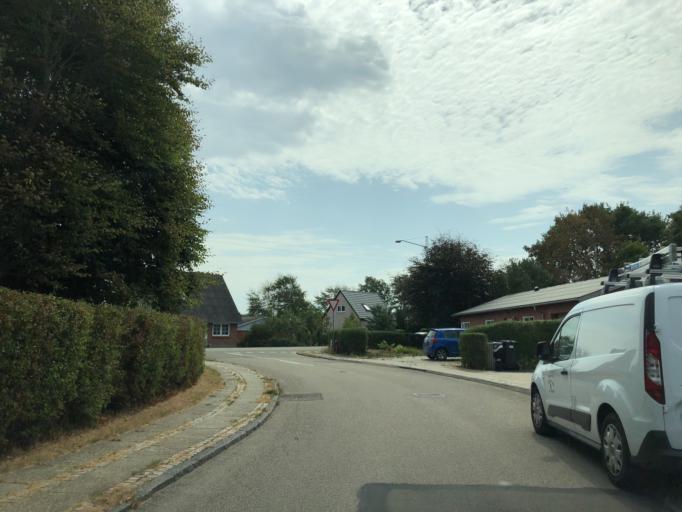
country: DK
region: Central Jutland
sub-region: Ringkobing-Skjern Kommune
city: Tarm
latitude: 55.9000
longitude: 8.5151
